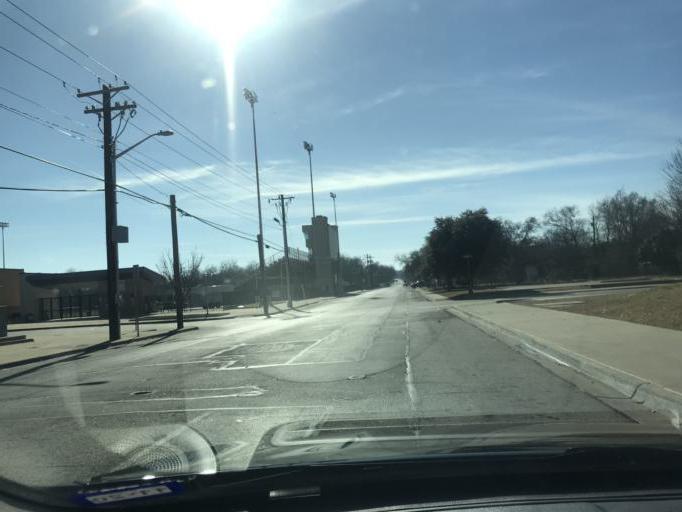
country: US
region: Texas
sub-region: Denton County
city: Denton
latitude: 33.2238
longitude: -97.1433
